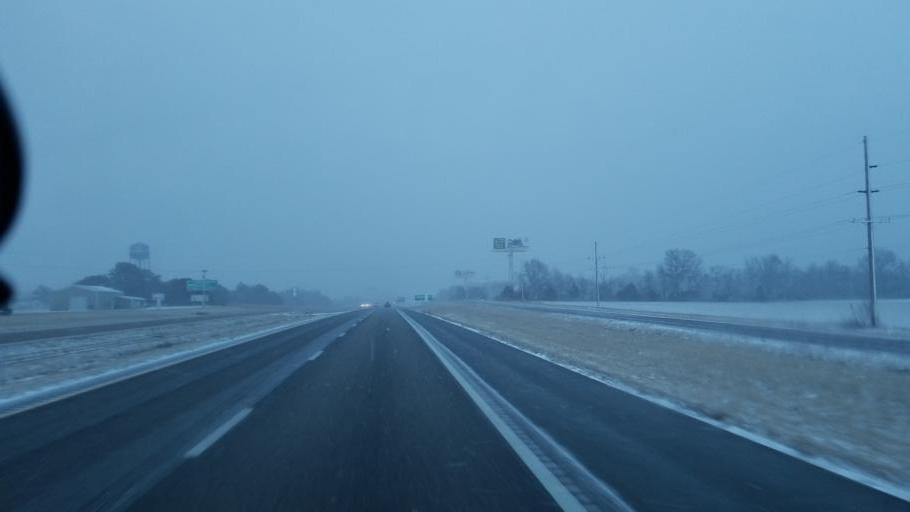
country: US
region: Missouri
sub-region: Montgomery County
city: Montgomery City
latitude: 38.9025
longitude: -91.4740
